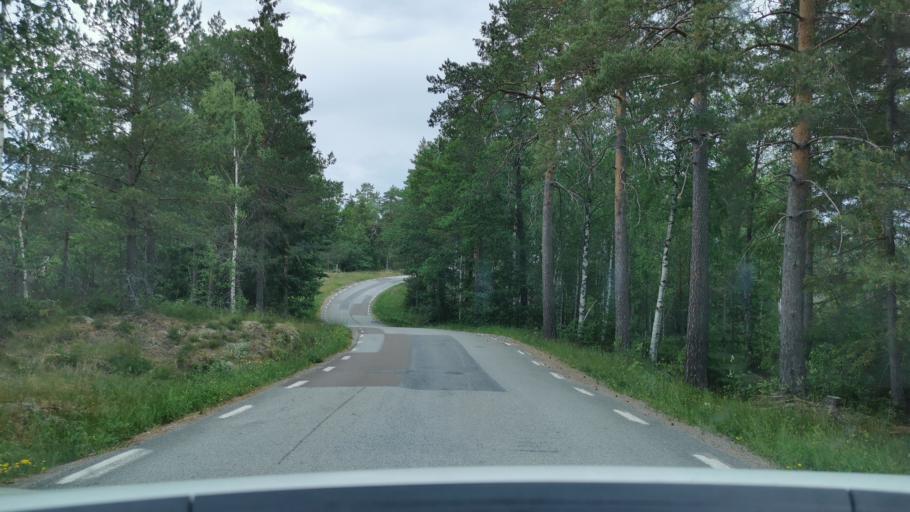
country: SE
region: Vaestra Goetaland
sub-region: Bengtsfors Kommun
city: Dals Langed
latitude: 58.8697
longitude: 12.4025
